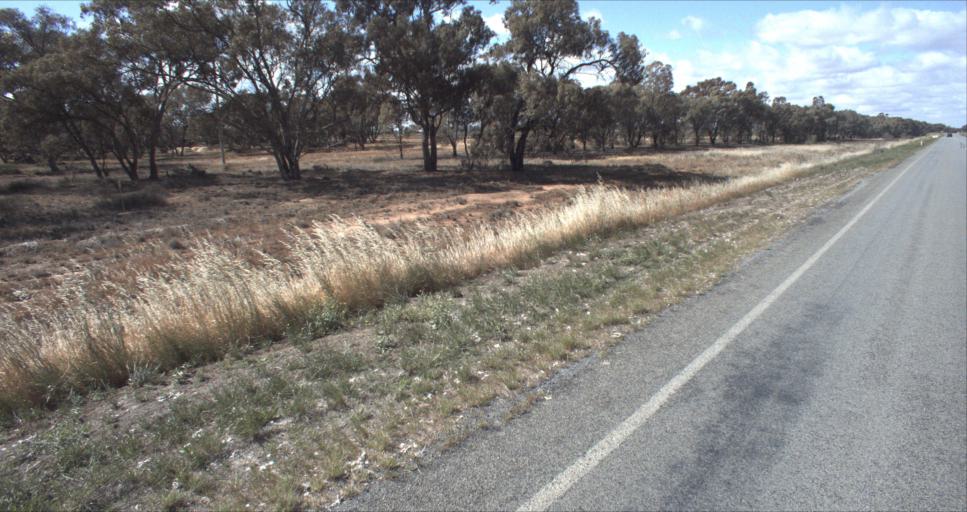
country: AU
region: New South Wales
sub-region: Murrumbidgee Shire
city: Darlington Point
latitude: -34.5465
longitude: 146.1713
